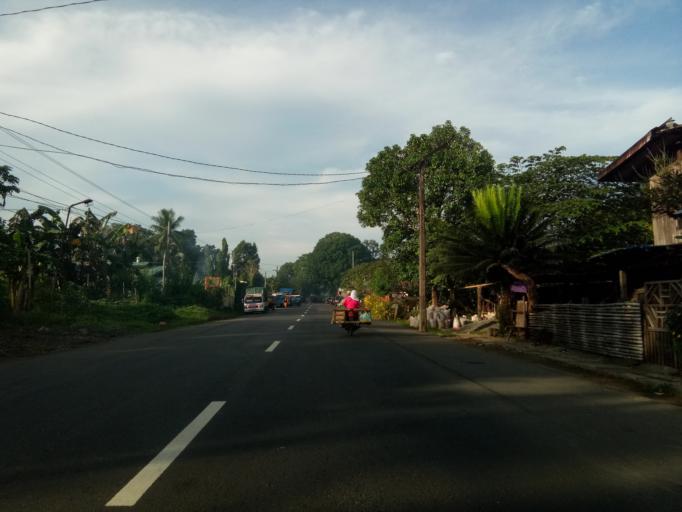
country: PH
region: Caraga
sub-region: Province of Surigao del Norte
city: Tubod
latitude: 9.5574
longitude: 125.5694
